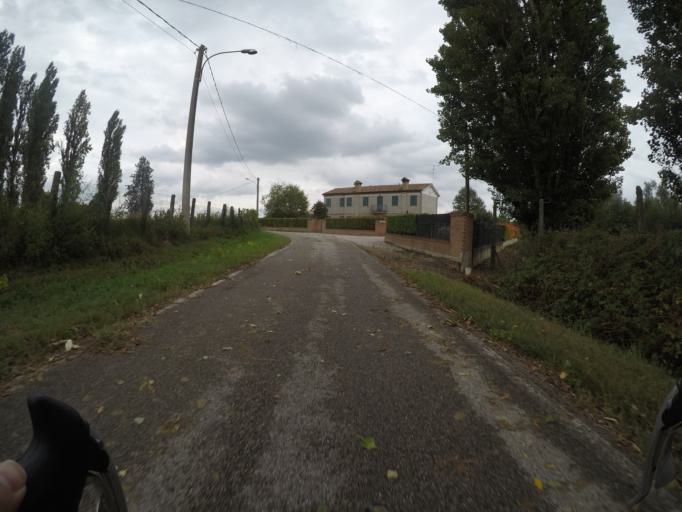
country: IT
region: Veneto
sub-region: Provincia di Rovigo
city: Polesella
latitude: 44.9604
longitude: 11.7295
